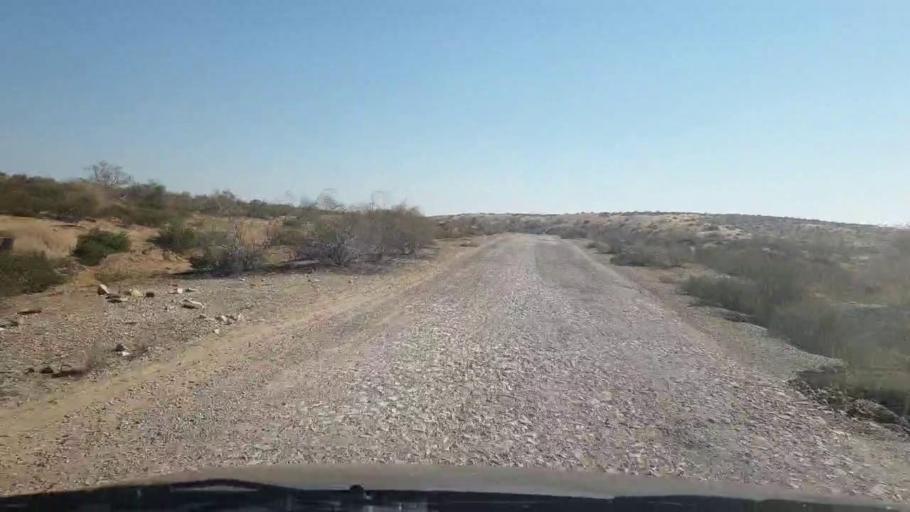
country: PK
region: Sindh
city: Bozdar
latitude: 27.0160
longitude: 68.7360
